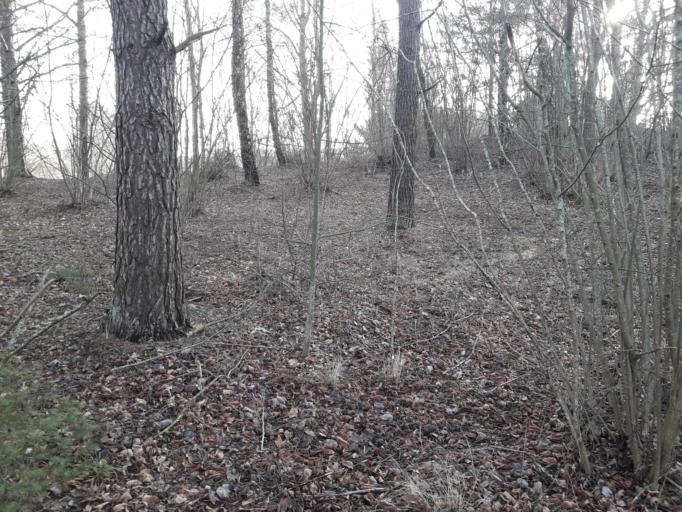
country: LT
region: Alytaus apskritis
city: Druskininkai
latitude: 54.1303
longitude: 24.0331
